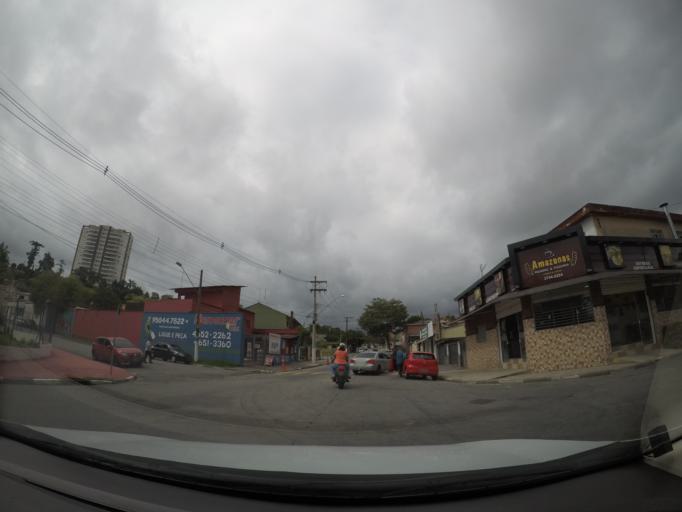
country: BR
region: Sao Paulo
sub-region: Aruja
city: Aruja
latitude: -23.3942
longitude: -46.3147
